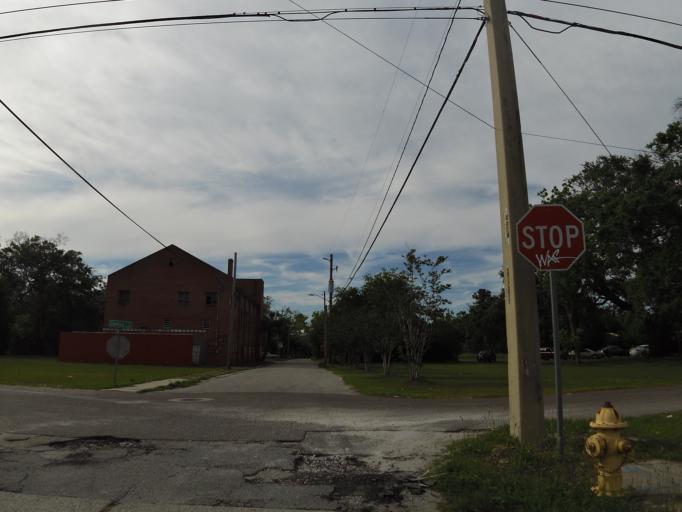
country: US
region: Florida
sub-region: Duval County
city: Jacksonville
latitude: 30.3243
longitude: -81.6754
